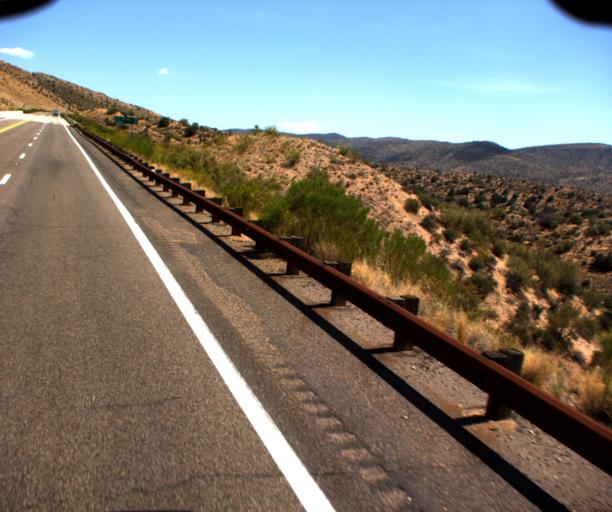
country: US
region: Arizona
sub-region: Gila County
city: Miami
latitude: 33.5626
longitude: -110.9526
